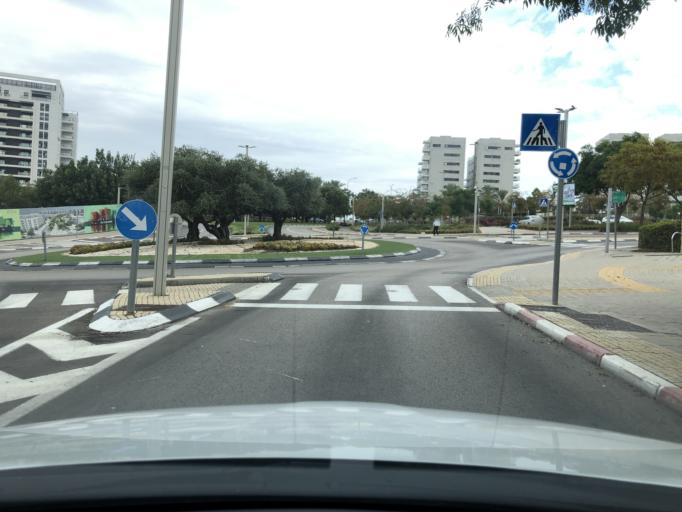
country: IL
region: Central District
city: Modiin
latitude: 31.9074
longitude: 35.0073
